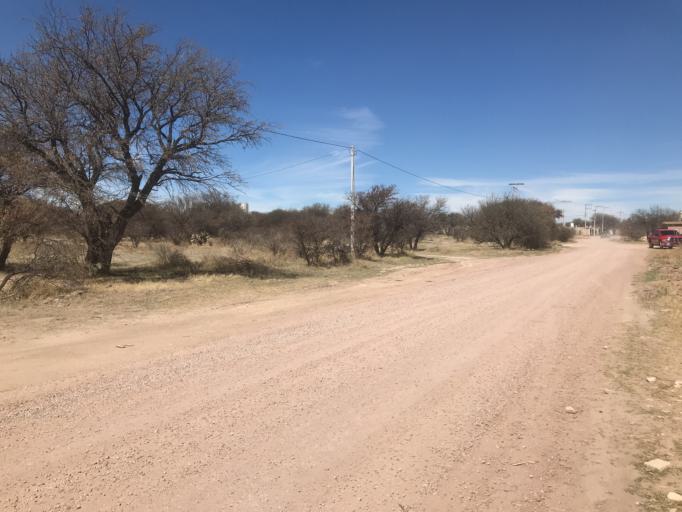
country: MX
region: Durango
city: Victoria de Durango
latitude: 24.0121
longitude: -104.5893
